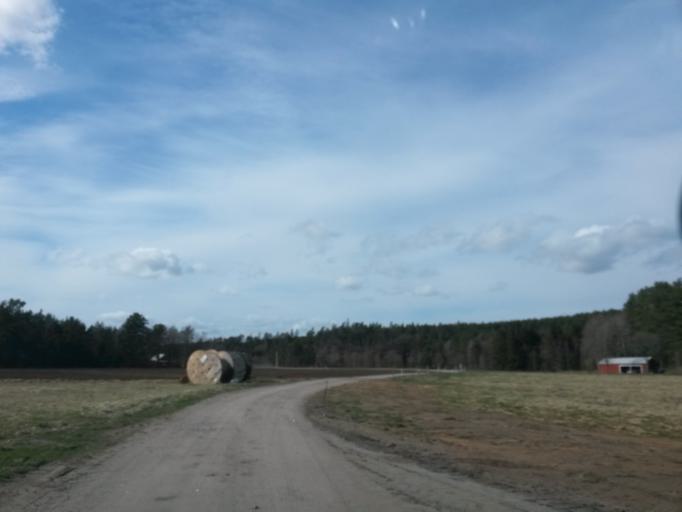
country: SE
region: Vaestra Goetaland
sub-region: Vargarda Kommun
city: Jonstorp
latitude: 57.9435
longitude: 12.6980
